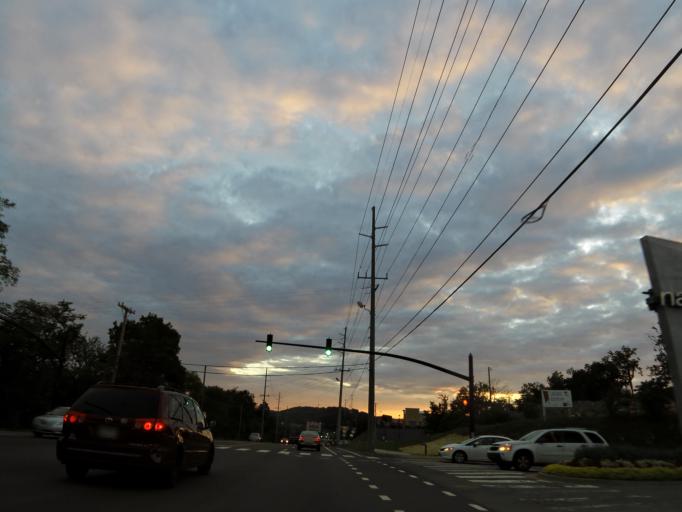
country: US
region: Tennessee
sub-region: Davidson County
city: Belle Meade
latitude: 36.1333
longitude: -86.8919
